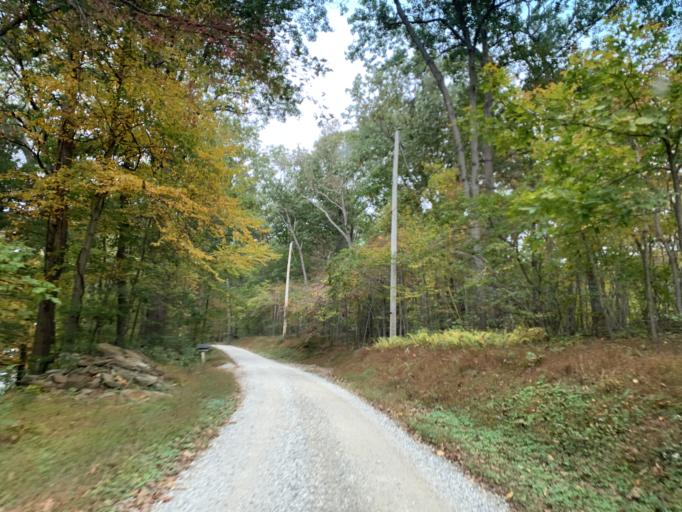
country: US
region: Pennsylvania
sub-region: York County
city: Susquehanna Trails
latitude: 39.7980
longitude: -76.4287
